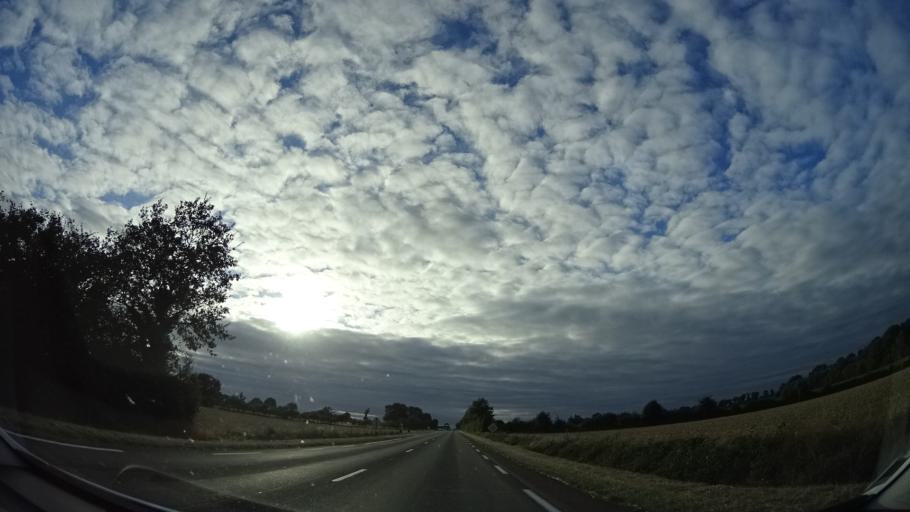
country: FR
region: Pays de la Loire
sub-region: Departement de la Sarthe
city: Saint-Calais
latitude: 47.9400
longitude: 0.6768
